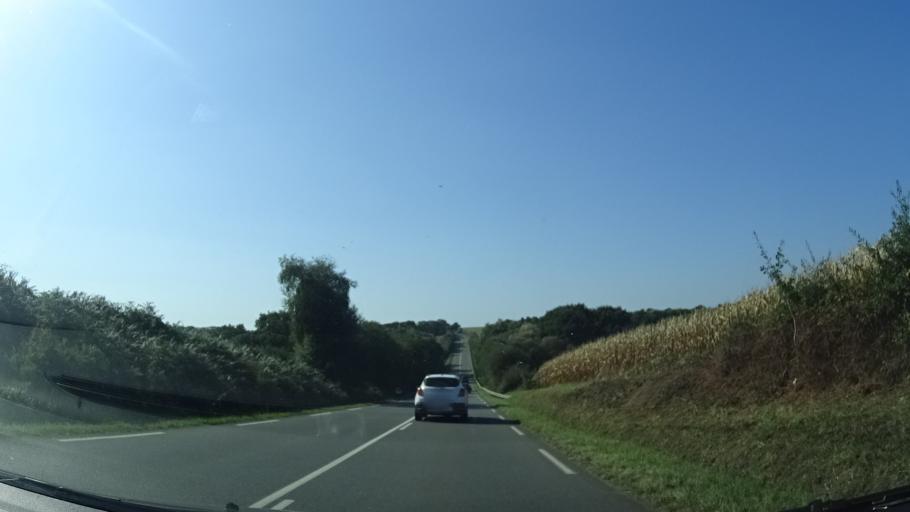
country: FR
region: Brittany
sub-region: Departement du Finistere
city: Plonevez-Porzay
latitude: 48.1126
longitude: -4.2403
